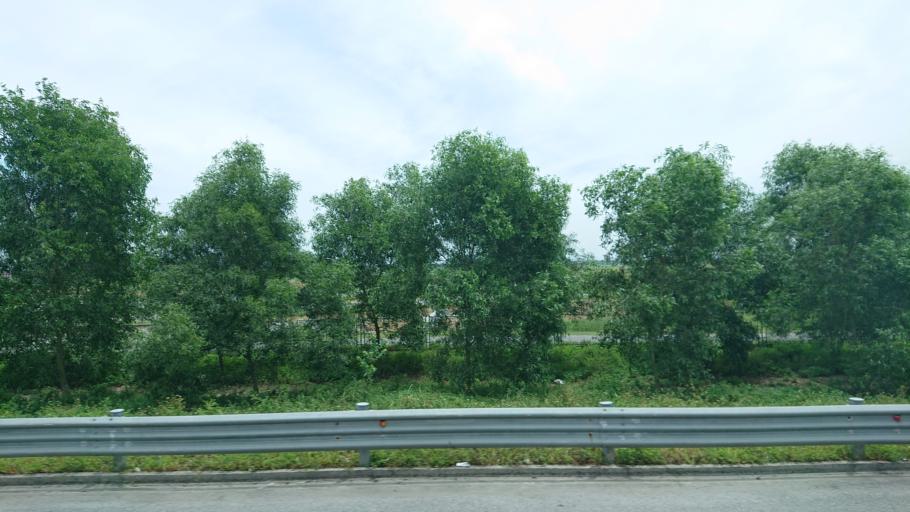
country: VN
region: Hai Phong
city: Nui Doi
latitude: 20.7659
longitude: 106.6518
